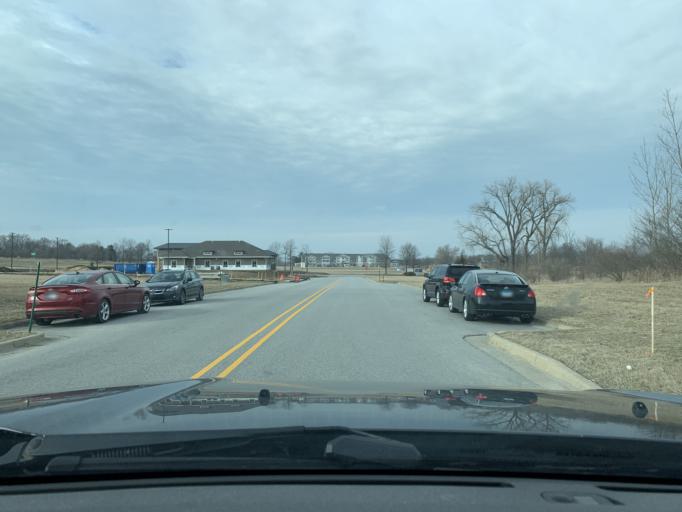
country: US
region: Indiana
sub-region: Porter County
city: Chesterton
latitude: 41.5803
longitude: -87.0426
